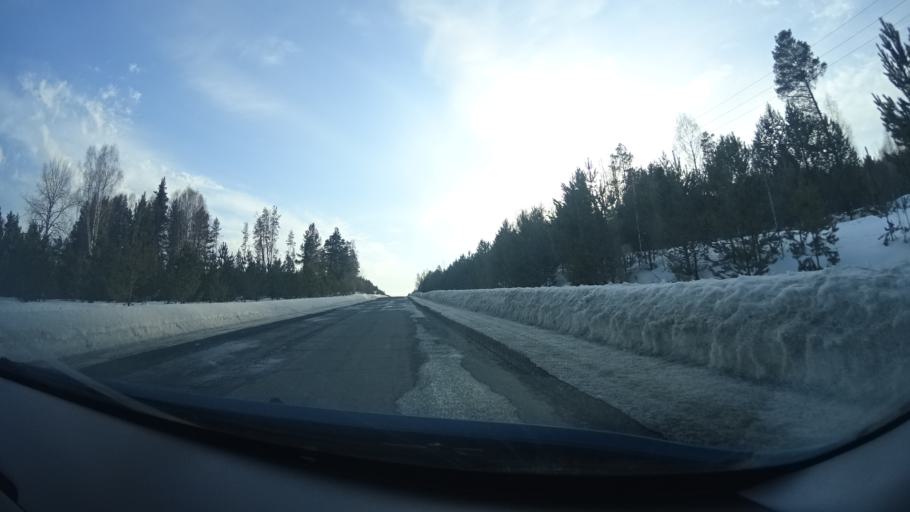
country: RU
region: Bashkortostan
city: Lomovka
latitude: 53.6548
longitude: 58.2123
